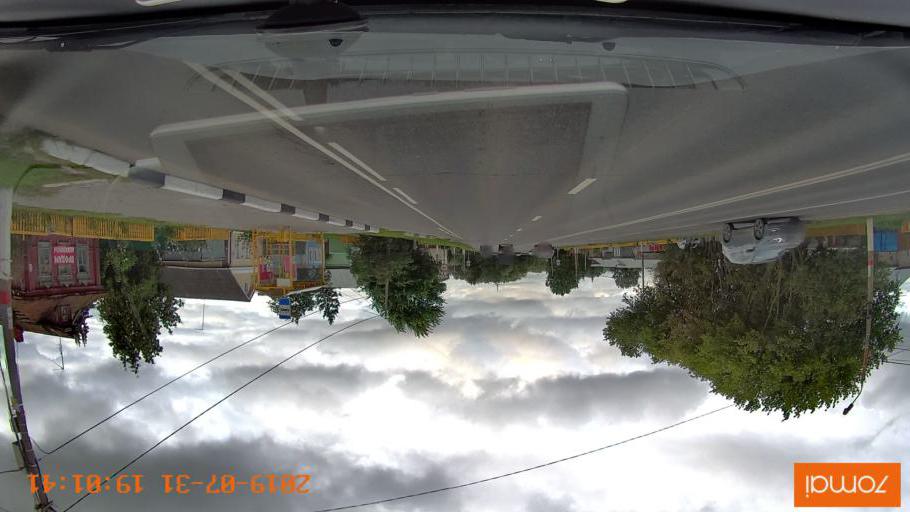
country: RU
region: Moskovskaya
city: Raduzhnyy
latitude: 55.1248
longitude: 38.7292
